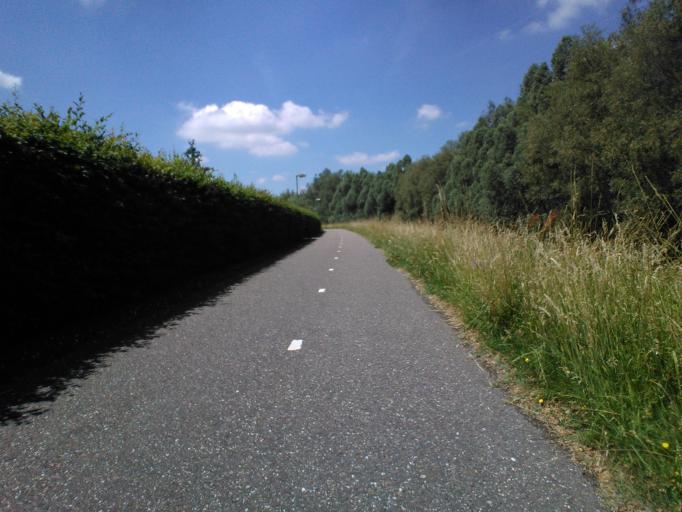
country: NL
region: South Holland
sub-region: Gemeente Gorinchem
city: Gorinchem
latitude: 51.8207
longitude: 4.9538
